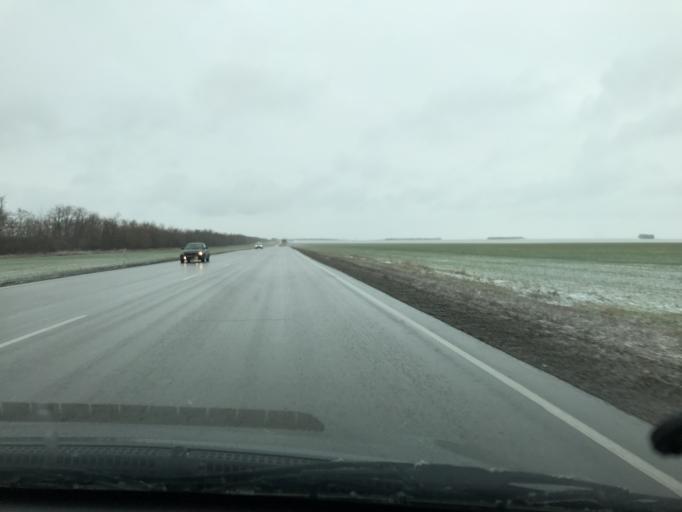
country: RU
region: Rostov
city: Kagal'nitskaya
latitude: 46.9123
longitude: 40.1123
